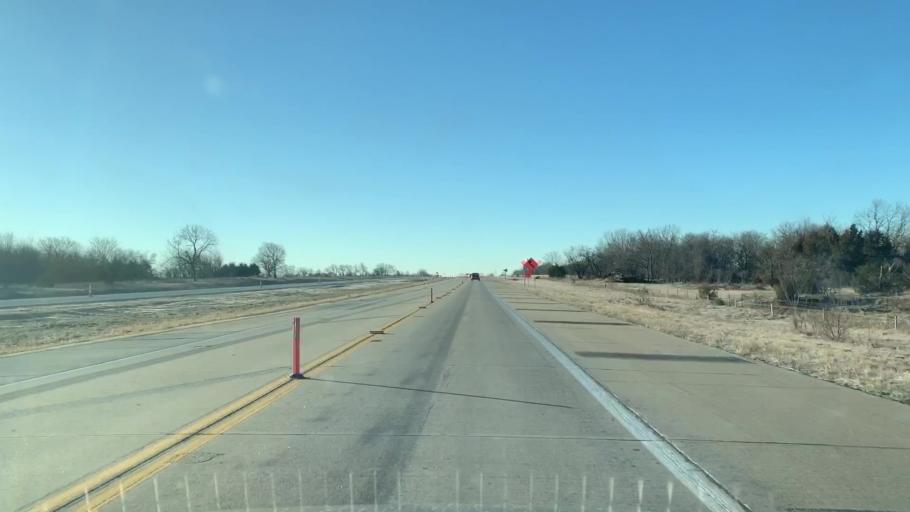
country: US
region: Kansas
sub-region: Bourbon County
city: Fort Scott
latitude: 37.7563
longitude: -94.7051
